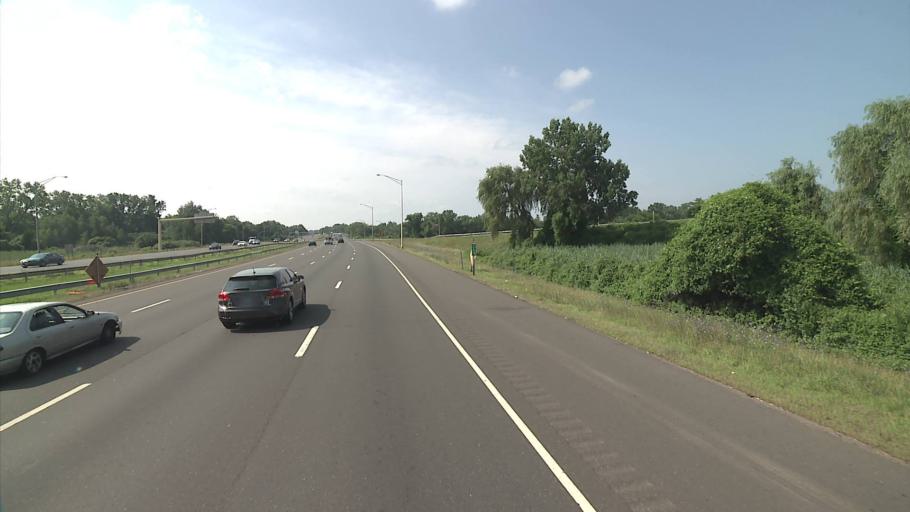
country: US
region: Connecticut
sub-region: New Haven County
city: North Haven
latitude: 41.3756
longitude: -72.8694
